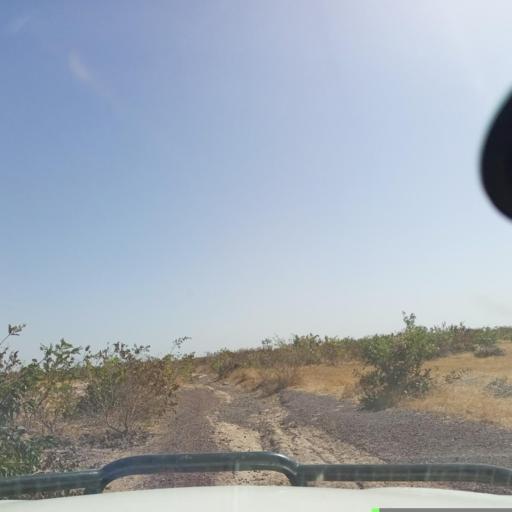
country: ML
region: Koulikoro
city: Dioila
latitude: 12.6540
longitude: -7.1108
